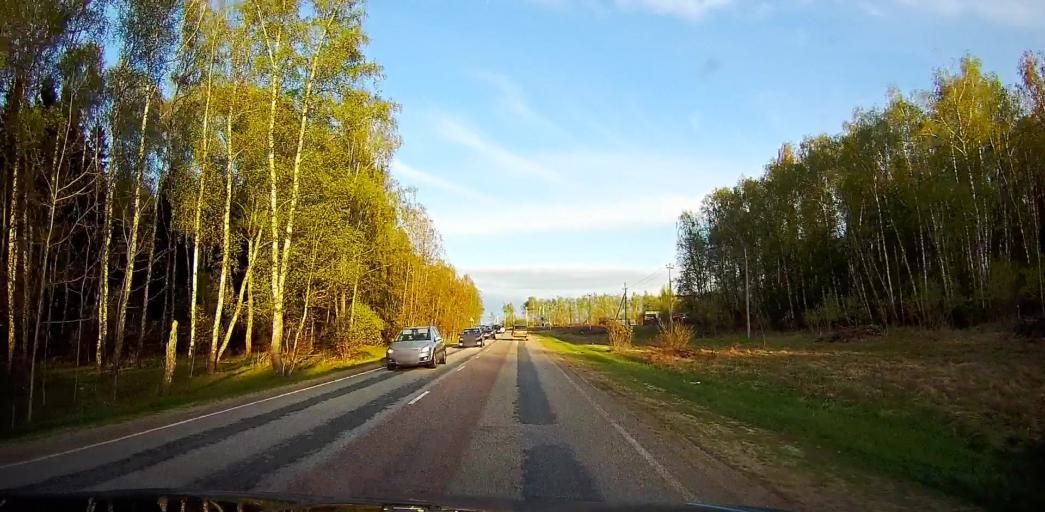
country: RU
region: Moskovskaya
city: Meshcherino
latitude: 55.2245
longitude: 38.3962
